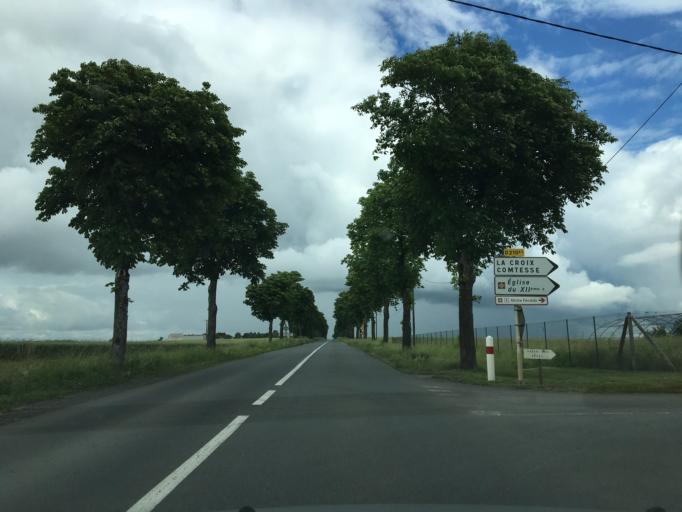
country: FR
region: Poitou-Charentes
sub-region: Departement des Deux-Sevres
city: Beauvoir-sur-Niort
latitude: 46.0774
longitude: -0.5061
